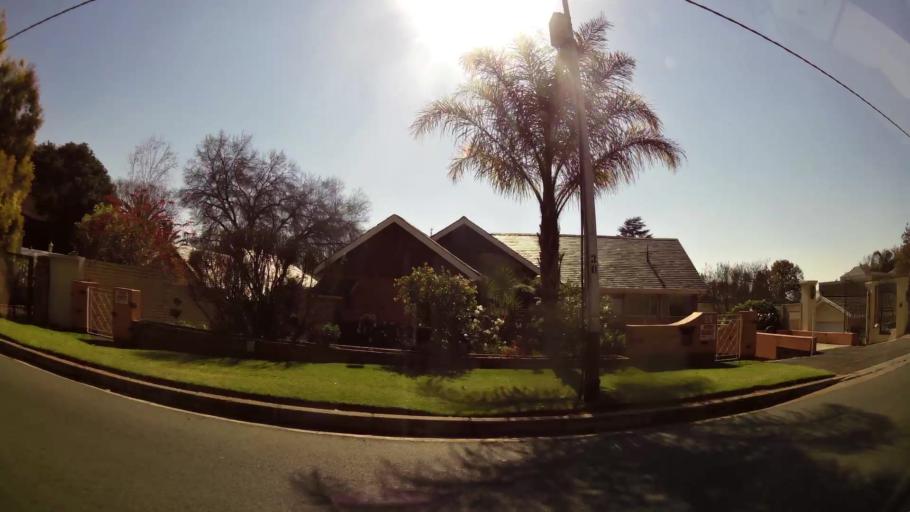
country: ZA
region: Gauteng
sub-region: City of Johannesburg Metropolitan Municipality
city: Johannesburg
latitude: -26.1657
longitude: 28.1007
